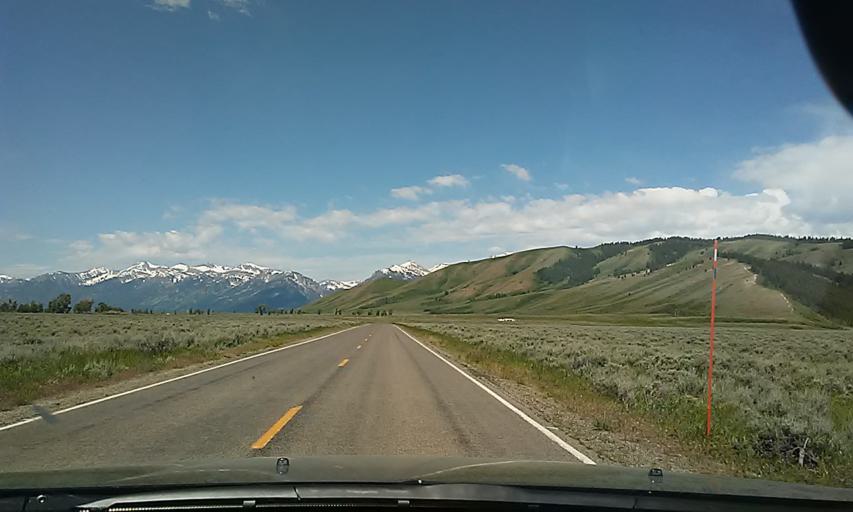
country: US
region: Wyoming
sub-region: Teton County
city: Jackson
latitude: 43.6252
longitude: -110.6555
